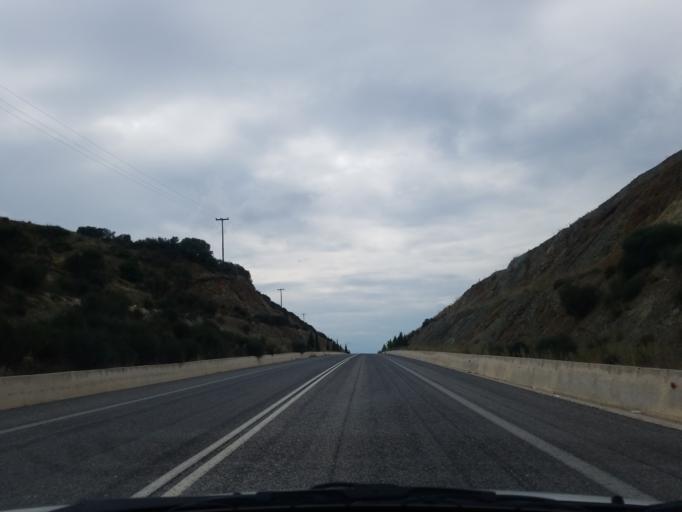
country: GR
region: Central Greece
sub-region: Nomos Fthiotidos
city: Domokos
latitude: 39.1052
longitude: 22.3067
